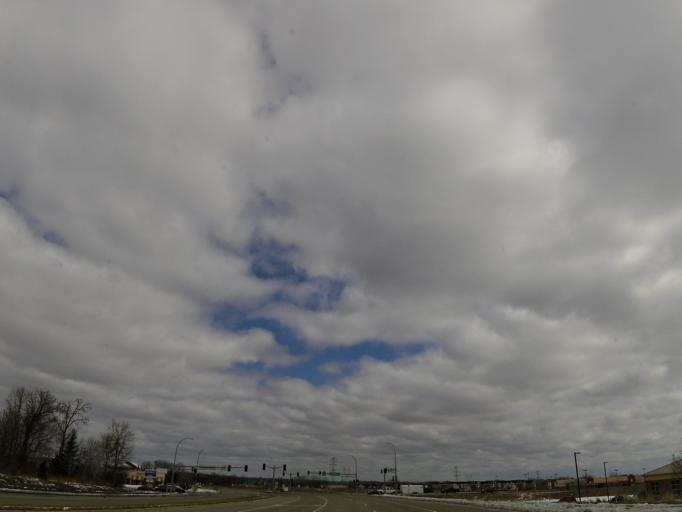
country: US
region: Minnesota
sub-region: Scott County
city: Prior Lake
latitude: 44.7731
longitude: -93.4165
